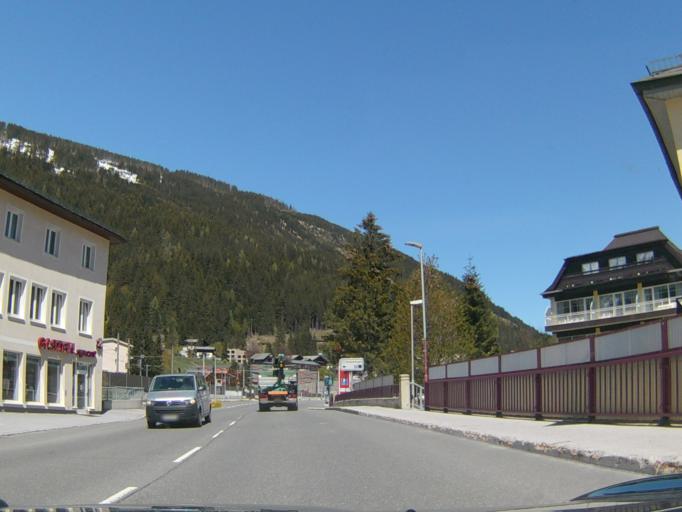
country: AT
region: Salzburg
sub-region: Politischer Bezirk Sankt Johann im Pongau
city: Bad Gastein
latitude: 47.1087
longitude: 13.1346
